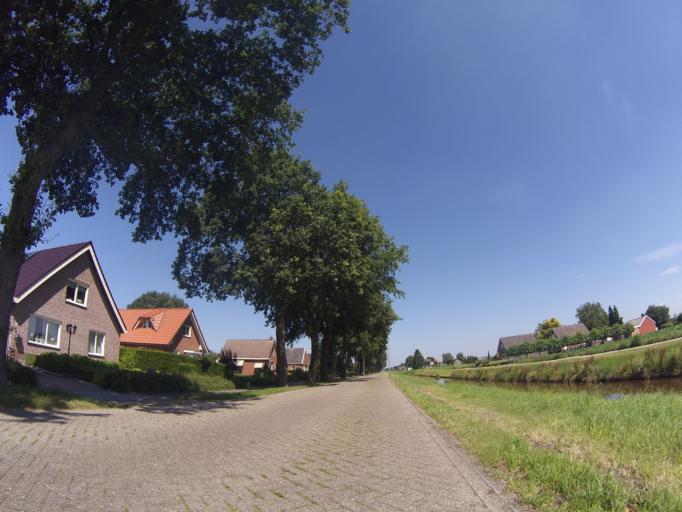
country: NL
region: Drenthe
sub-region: Gemeente Emmen
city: Klazienaveen
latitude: 52.7137
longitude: 7.0463
